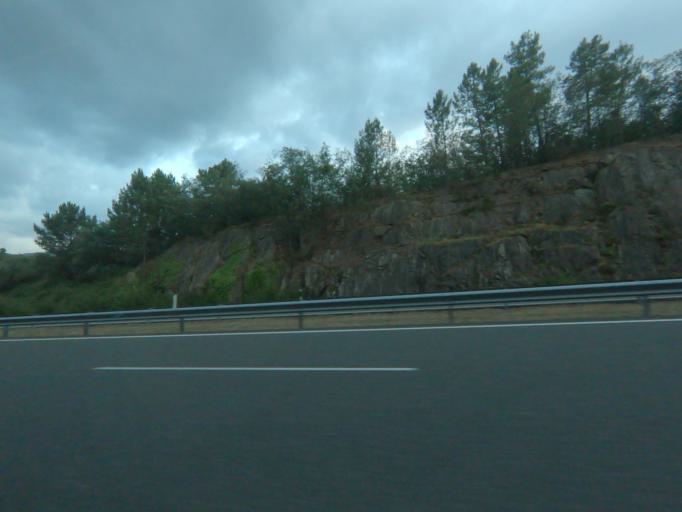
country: ES
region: Galicia
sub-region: Provincia de Ourense
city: Ribadavia
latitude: 42.3036
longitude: -8.1450
